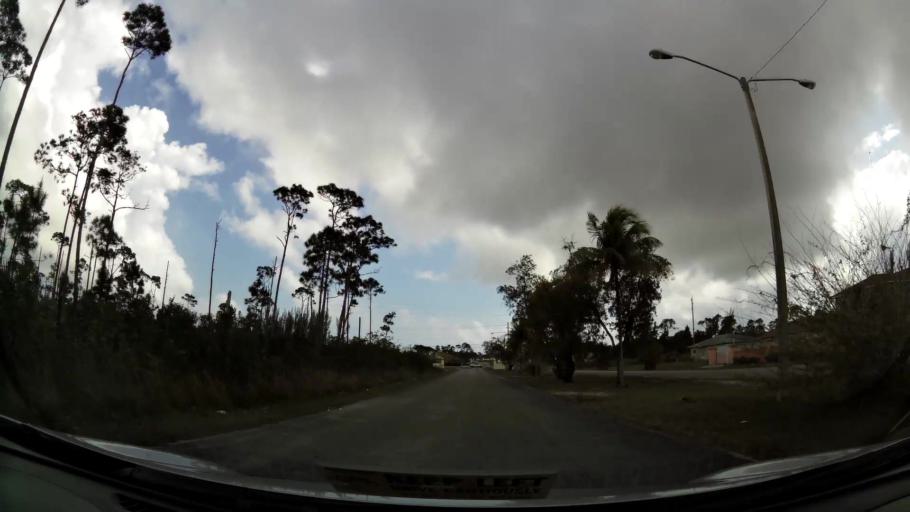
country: BS
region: Freeport
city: Freeport
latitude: 26.5183
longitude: -78.7223
